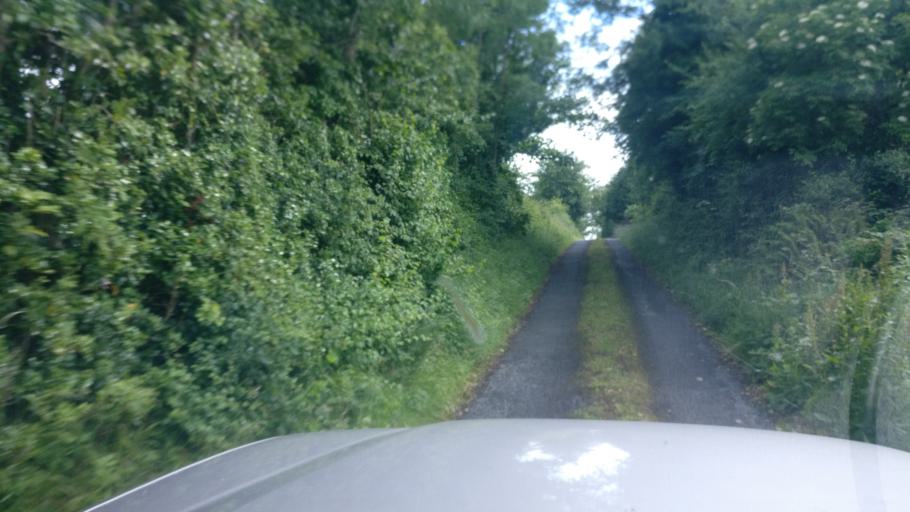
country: IE
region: Connaught
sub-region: County Galway
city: Gort
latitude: 53.0789
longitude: -8.7717
